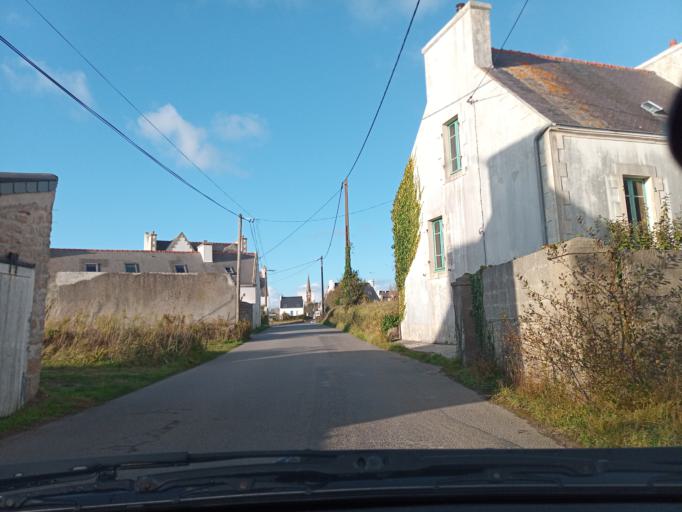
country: FR
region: Brittany
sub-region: Departement du Finistere
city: Esquibien
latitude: 48.0208
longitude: -4.5638
